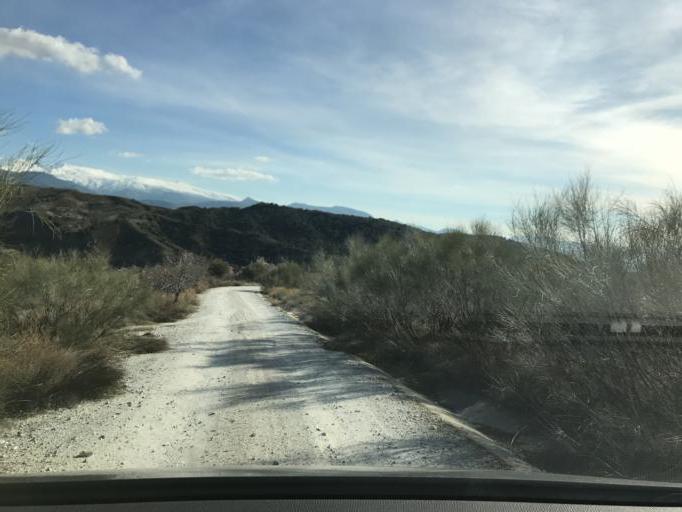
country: ES
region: Andalusia
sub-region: Provincia de Granada
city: Huetor Santillan
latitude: 37.2196
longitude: -3.5047
